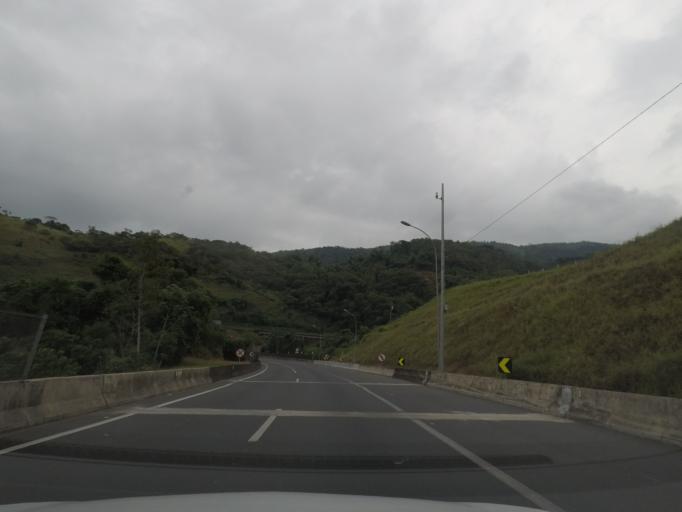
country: BR
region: Sao Paulo
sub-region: Miracatu
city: Miracatu
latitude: -24.1093
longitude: -47.2673
